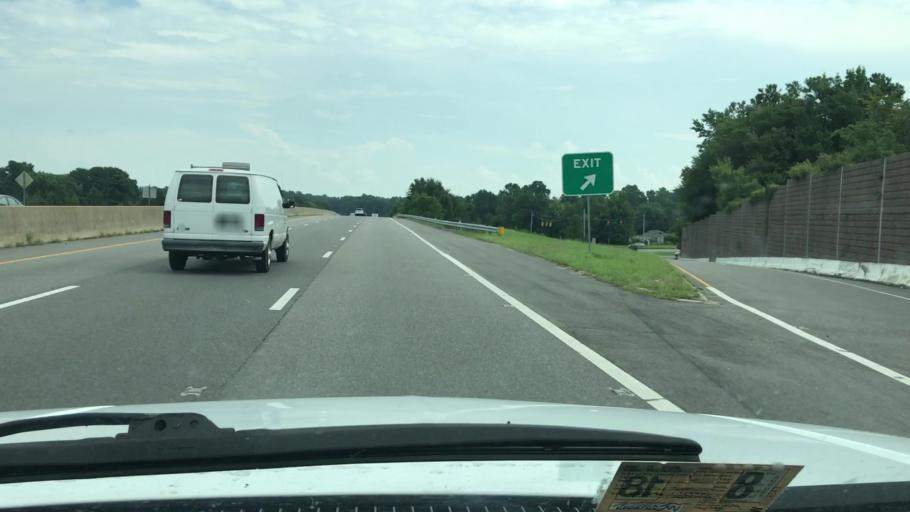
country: US
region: Virginia
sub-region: Chesterfield County
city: Bon Air
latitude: 37.4805
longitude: -77.5162
